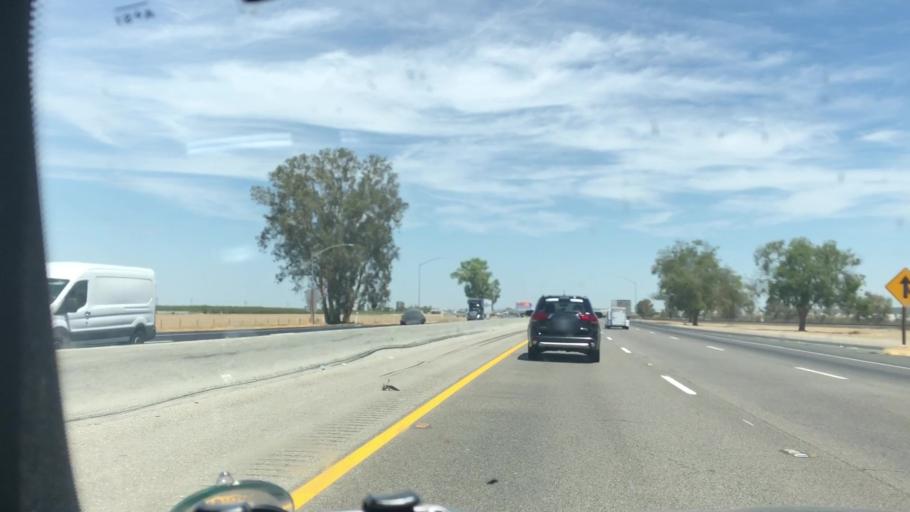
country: US
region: California
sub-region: Kern County
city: McFarland
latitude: 35.7201
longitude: -119.2375
